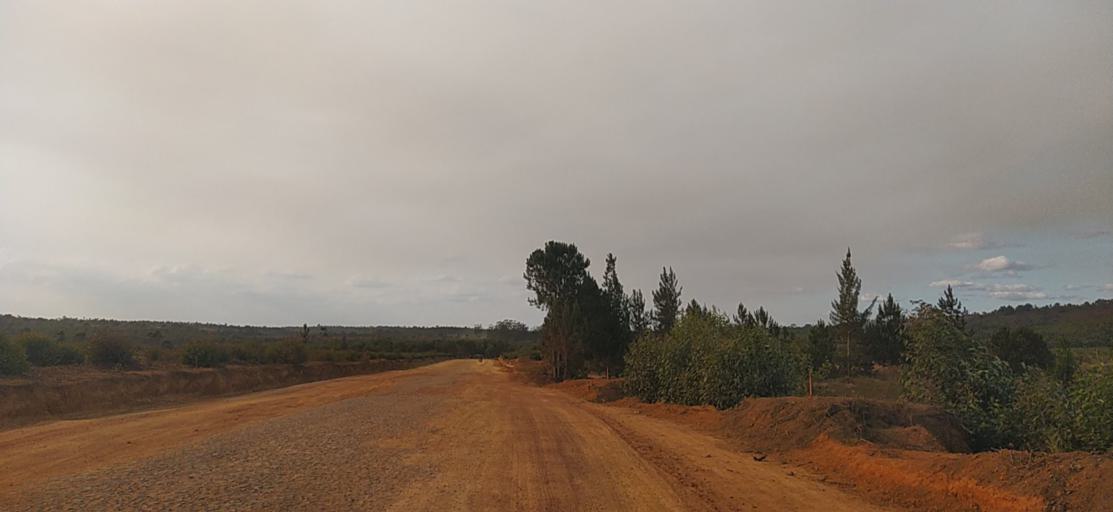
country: MG
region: Alaotra Mangoro
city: Moramanga
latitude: -18.5983
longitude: 48.2782
